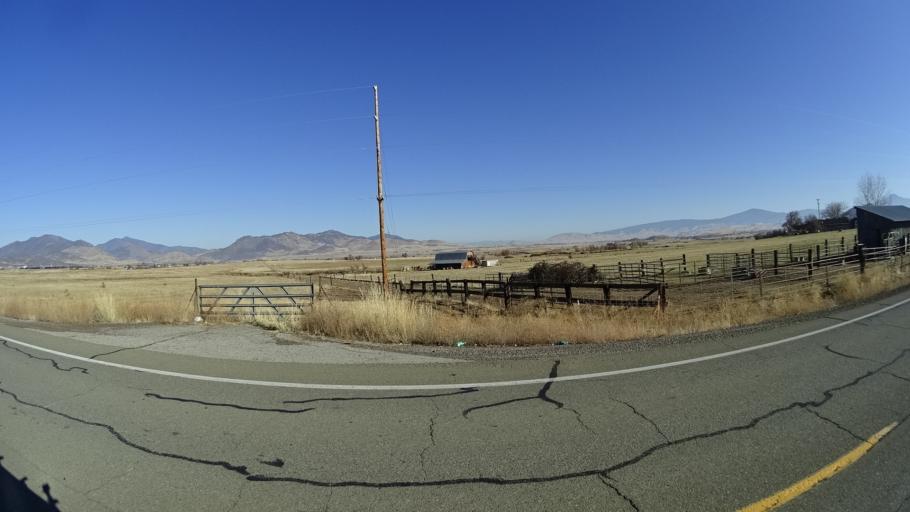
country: US
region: California
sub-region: Siskiyou County
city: Montague
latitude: 41.7095
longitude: -122.5743
